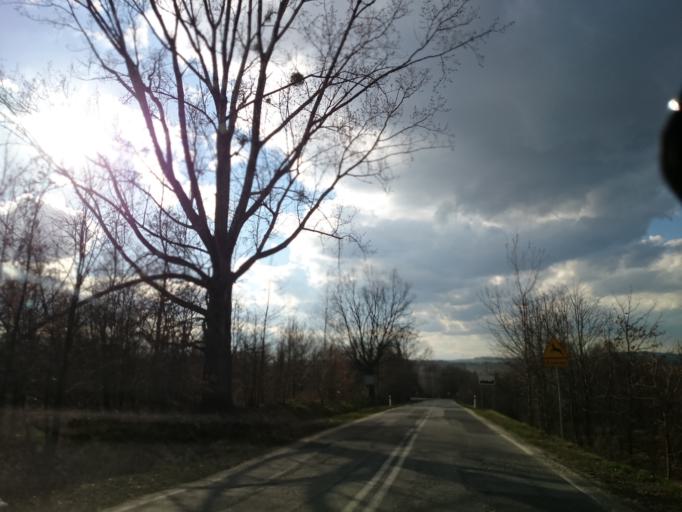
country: PL
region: Lower Silesian Voivodeship
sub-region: Powiat strzelinski
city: Przeworno
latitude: 50.6447
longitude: 17.1777
